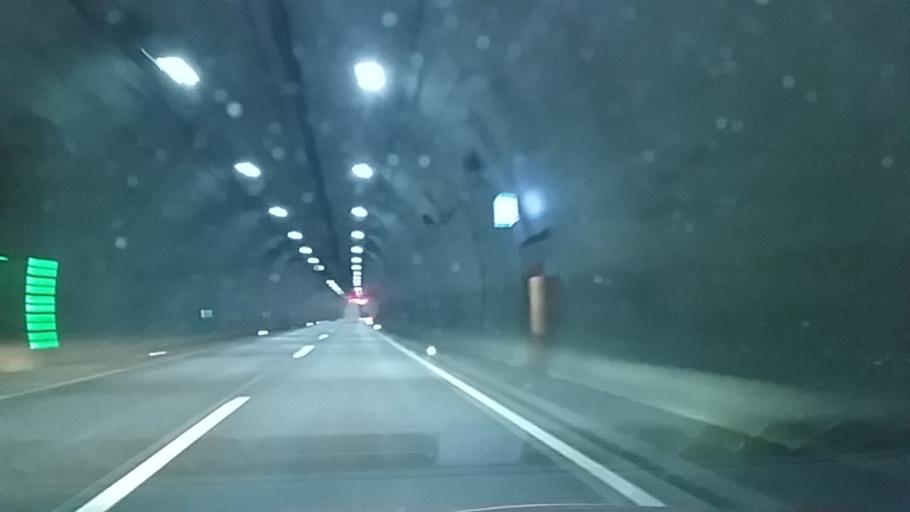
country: DE
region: Thuringia
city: Hemleben
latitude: 51.2732
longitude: 11.2153
